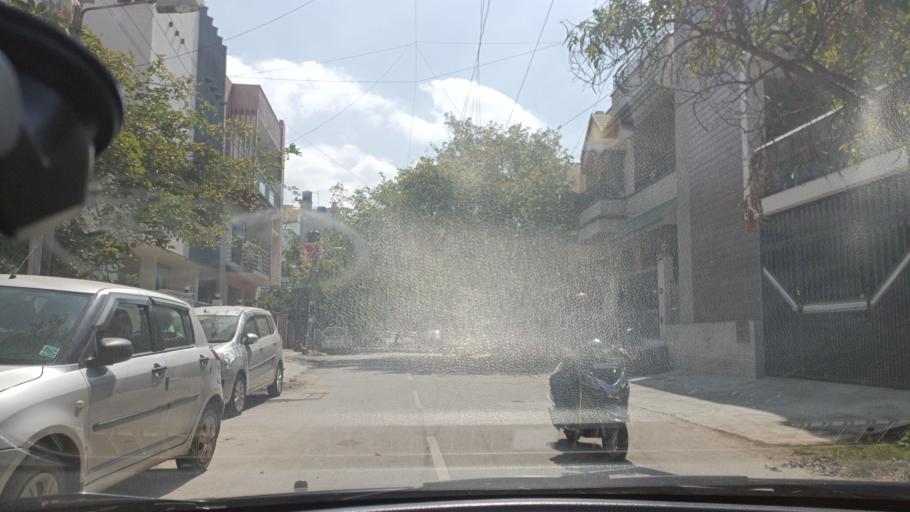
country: IN
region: Karnataka
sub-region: Bangalore Urban
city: Yelahanka
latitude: 13.0385
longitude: 77.6296
